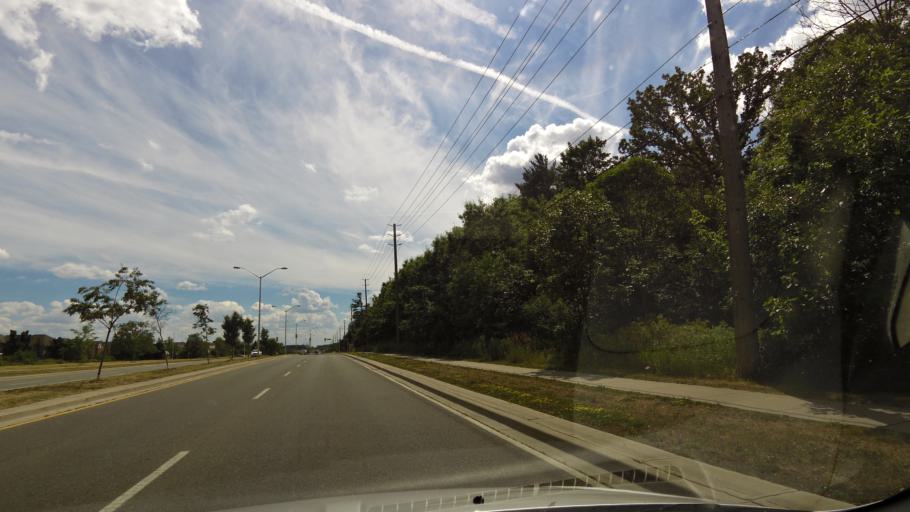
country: CA
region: Ontario
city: Oakville
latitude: 43.4332
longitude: -79.7482
